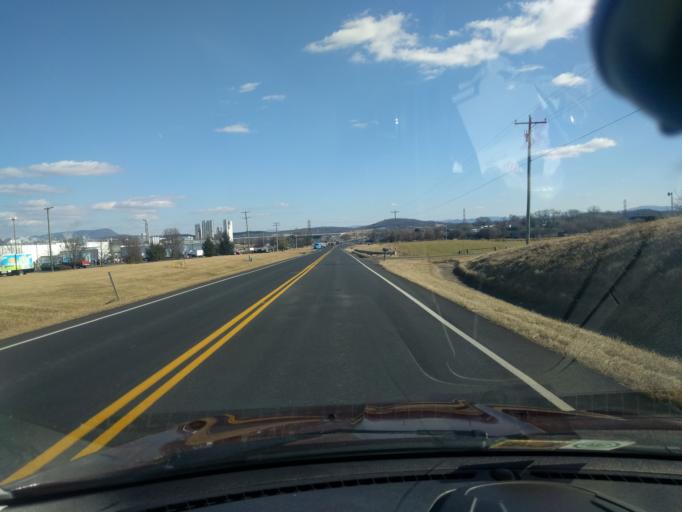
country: US
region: Virginia
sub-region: Rockingham County
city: Bridgewater
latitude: 38.3666
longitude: -78.9427
